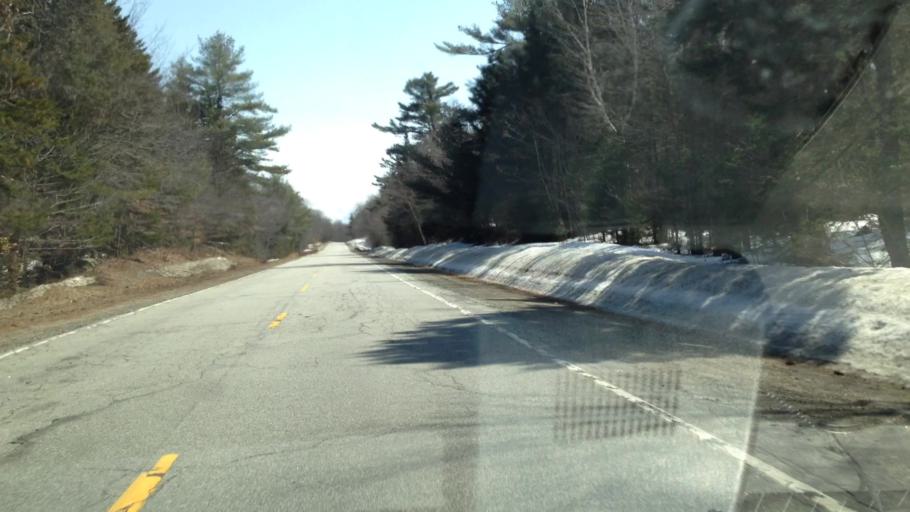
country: US
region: New Hampshire
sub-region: Sullivan County
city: Springfield
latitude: 43.4923
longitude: -71.9883
